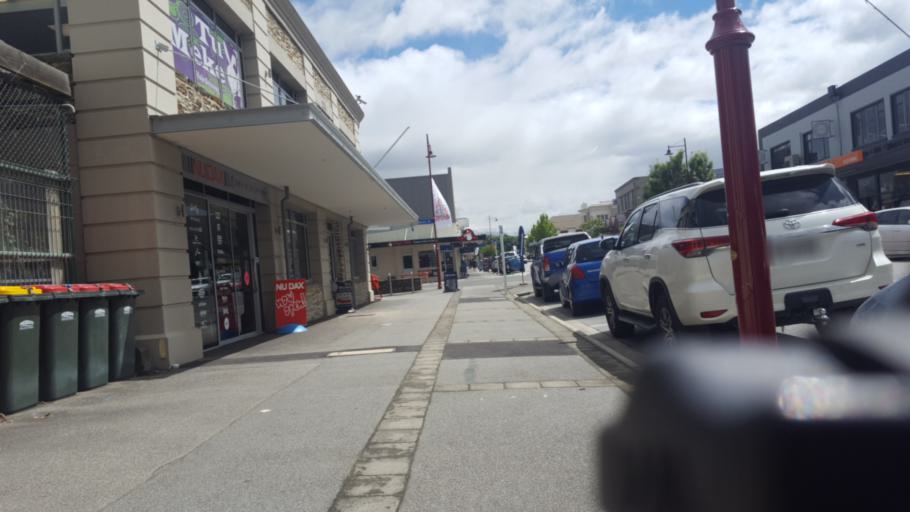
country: NZ
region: Otago
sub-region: Queenstown-Lakes District
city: Wanaka
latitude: -45.2580
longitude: 169.3929
